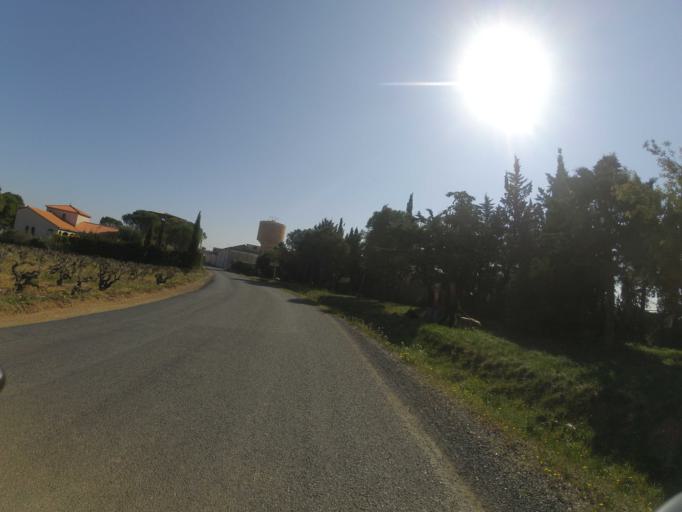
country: FR
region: Languedoc-Roussillon
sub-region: Departement des Pyrenees-Orientales
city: Llupia
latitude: 42.6096
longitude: 2.7678
